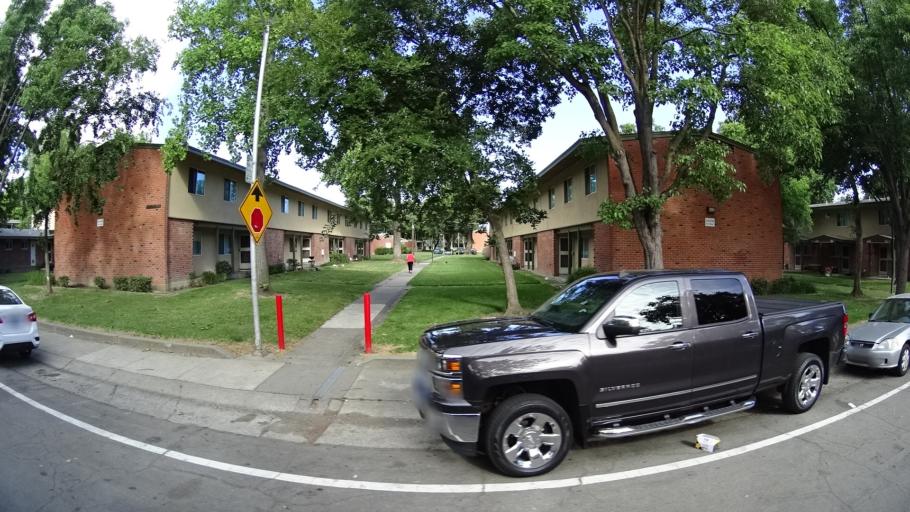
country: US
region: California
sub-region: Sacramento County
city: Sacramento
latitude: 38.5589
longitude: -121.5100
